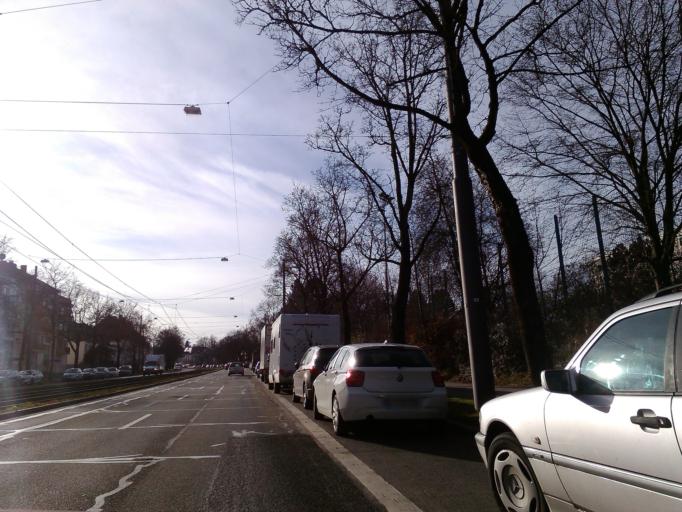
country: DE
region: Bavaria
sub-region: Upper Bavaria
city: Munich
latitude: 48.0998
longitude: 11.5658
